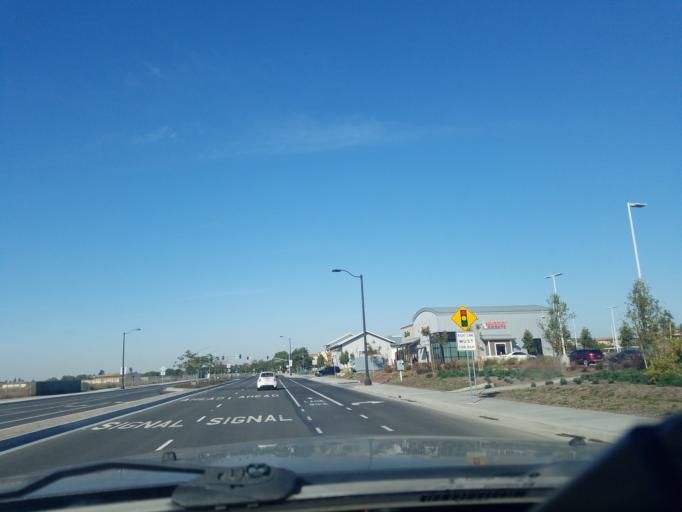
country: US
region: California
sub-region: Orange County
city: Tustin
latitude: 33.7102
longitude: -117.8171
